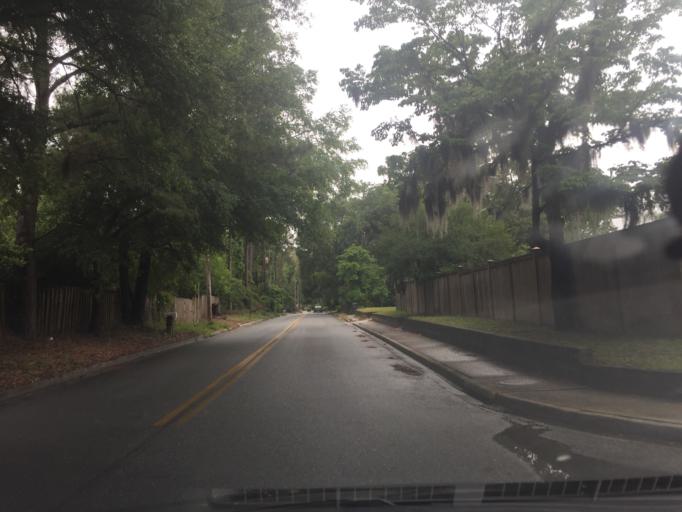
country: US
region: Georgia
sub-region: Chatham County
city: Isle of Hope
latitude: 31.9879
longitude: -81.0966
